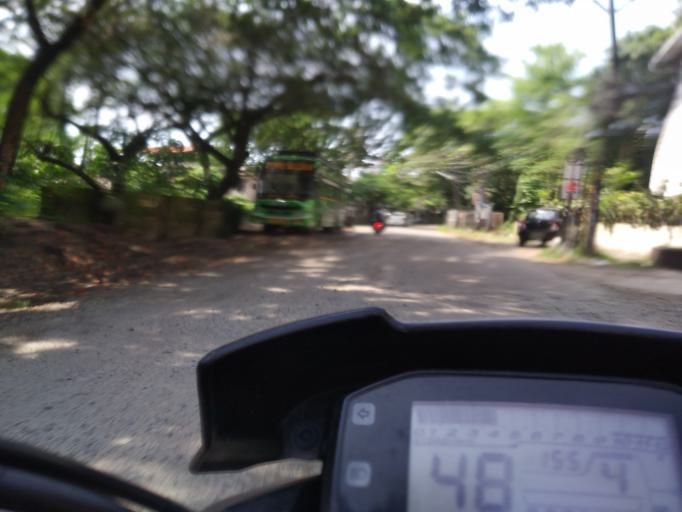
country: IN
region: Kerala
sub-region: Ernakulam
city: Cochin
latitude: 9.9749
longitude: 76.2953
